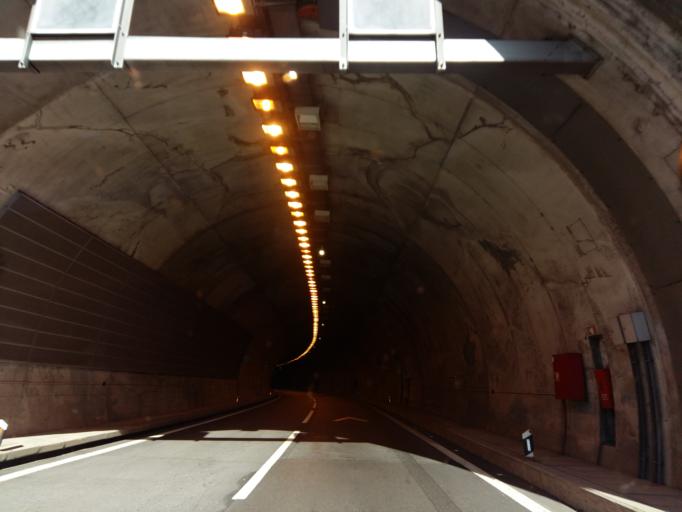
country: PT
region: Castelo Branco
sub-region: Concelho do Fundao
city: Fundao
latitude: 40.1036
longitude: -7.4692
